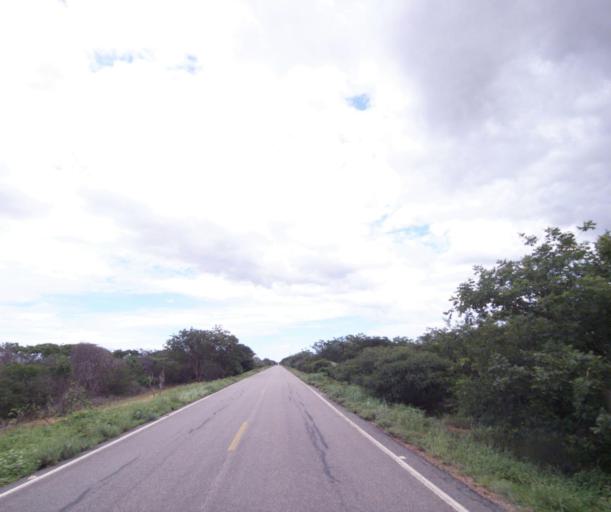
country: BR
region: Bahia
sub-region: Palmas De Monte Alto
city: Palmas de Monte Alto
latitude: -14.2622
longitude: -43.3174
